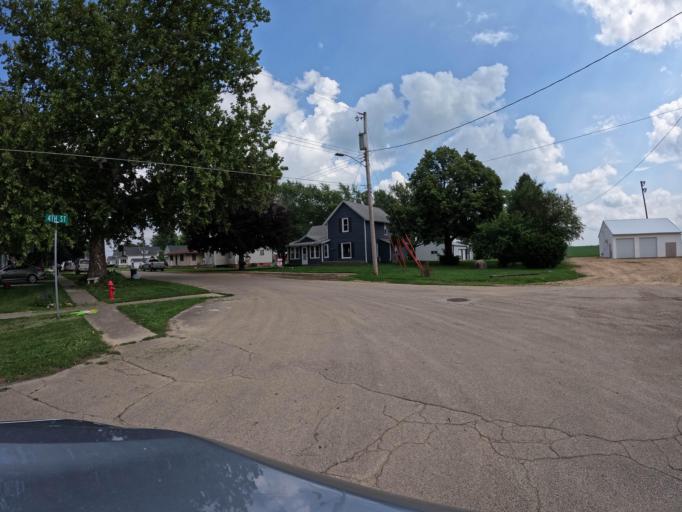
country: US
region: Iowa
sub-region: Clinton County
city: Camanche
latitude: 41.8001
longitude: -90.3577
